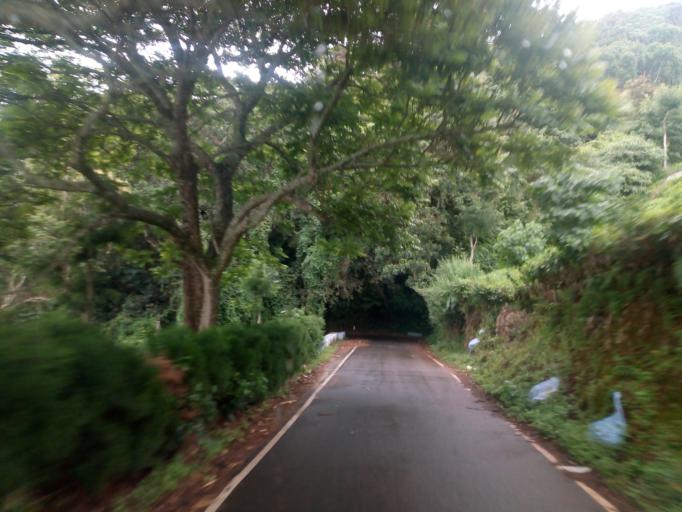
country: IN
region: Tamil Nadu
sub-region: Nilgiri
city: Wellington
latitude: 11.3611
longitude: 76.8414
